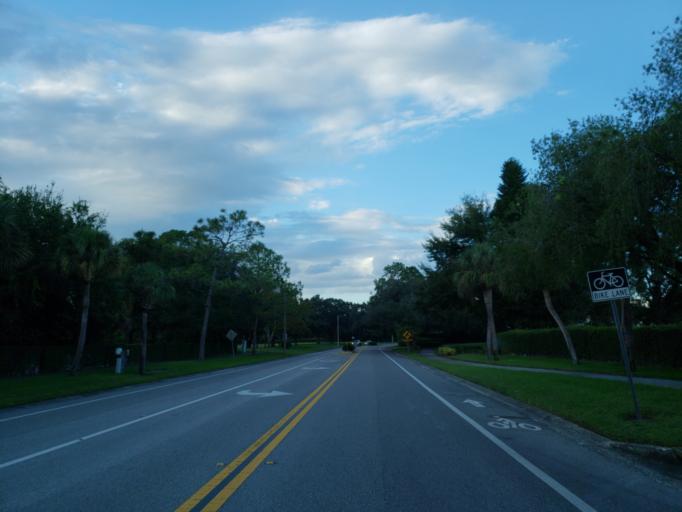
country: US
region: Florida
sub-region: Hillsborough County
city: Carrollwood Village
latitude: 28.0768
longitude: -82.5203
